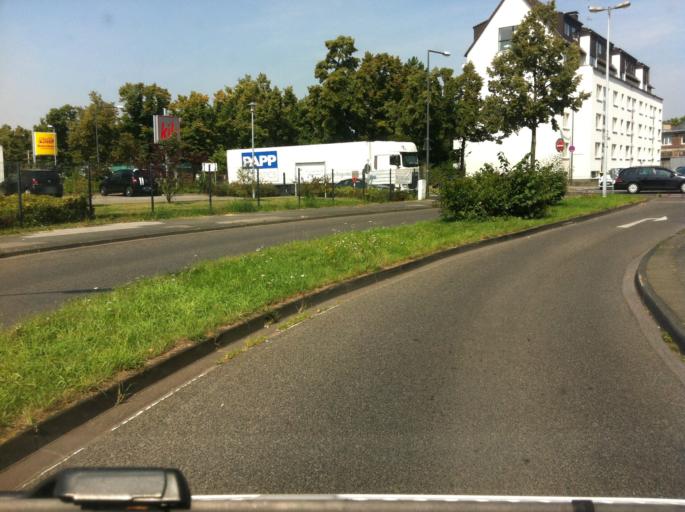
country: DE
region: North Rhine-Westphalia
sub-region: Regierungsbezirk Koln
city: Bilderstoeckchen
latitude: 50.9569
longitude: 6.8982
